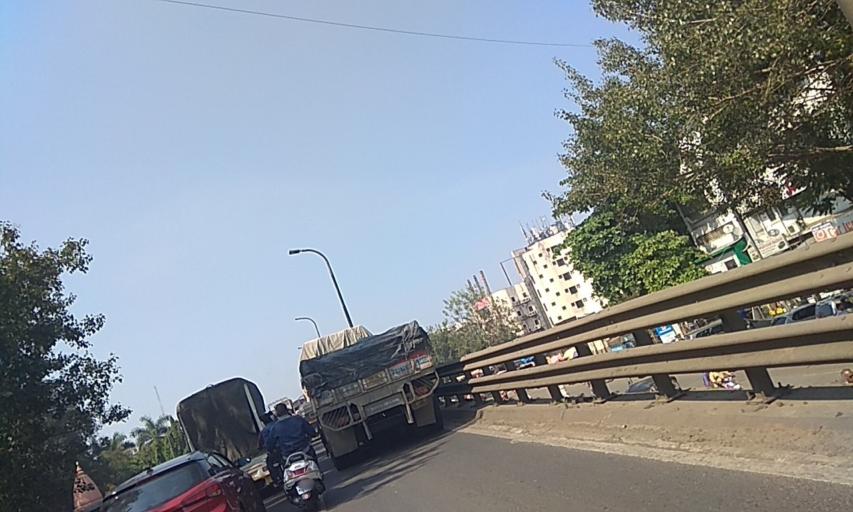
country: IN
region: Maharashtra
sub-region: Pune Division
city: Pune
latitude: 18.5020
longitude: 73.9290
